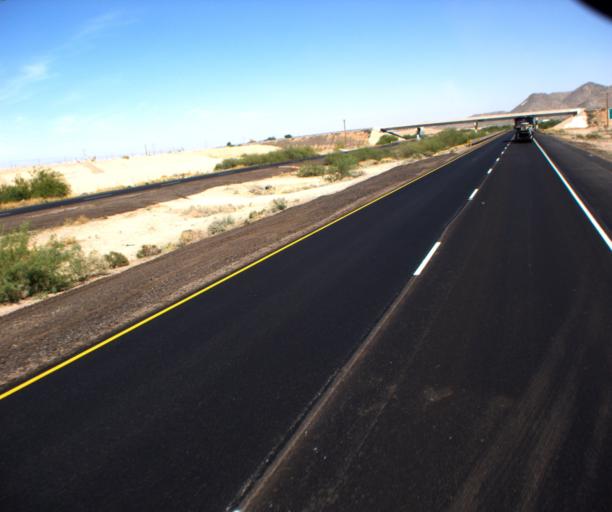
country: US
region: Arizona
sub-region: Pinal County
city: Casa Grande
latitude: 32.8279
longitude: -111.7602
